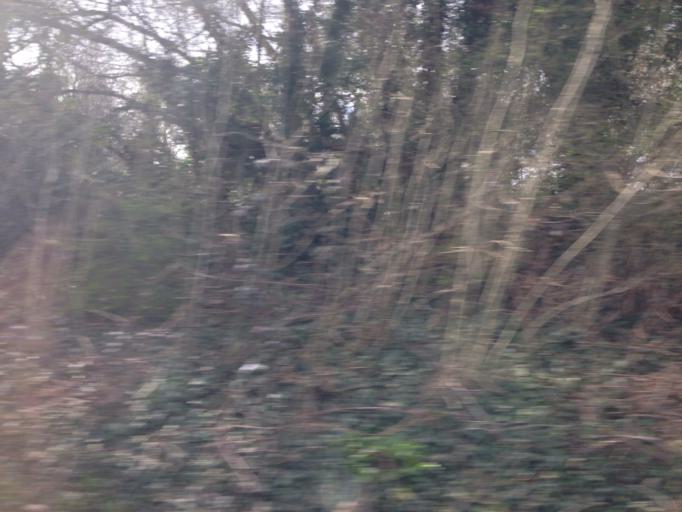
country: GB
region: England
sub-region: Greater London
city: Mitcham
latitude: 51.3972
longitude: -0.1606
